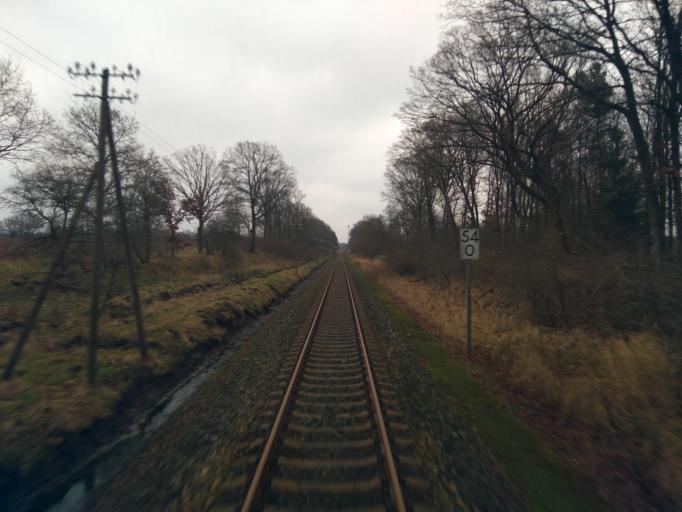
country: DE
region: Lower Saxony
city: Soltau
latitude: 52.9844
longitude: 9.8034
